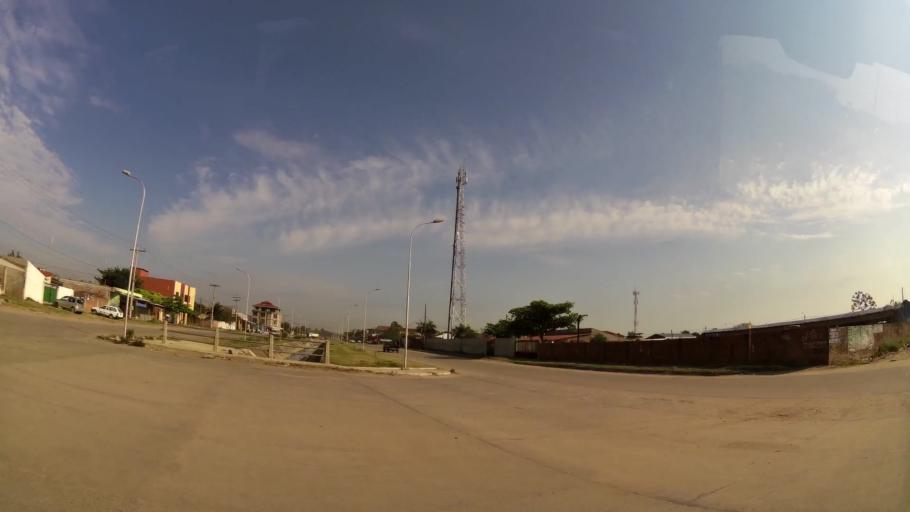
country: BO
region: Santa Cruz
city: Santa Cruz de la Sierra
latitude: -17.7279
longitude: -63.1368
